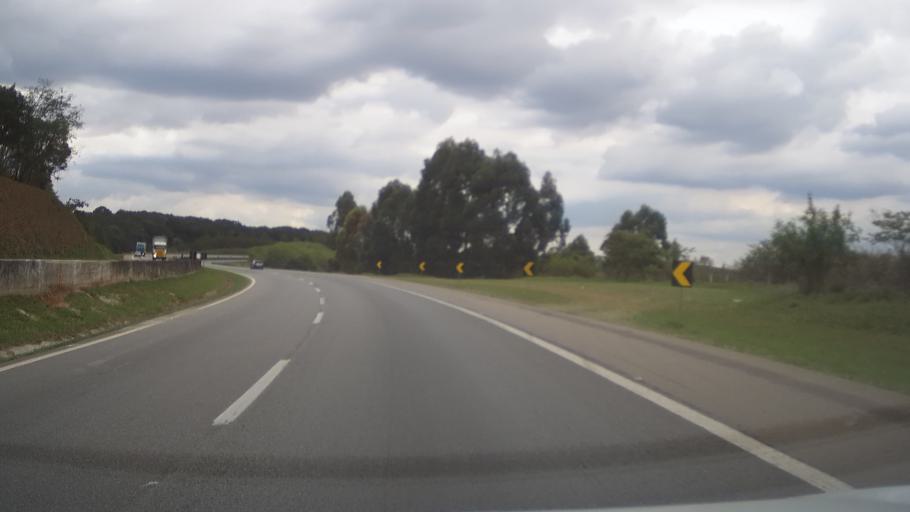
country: BR
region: Minas Gerais
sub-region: Tres Coracoes
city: Tres Coracoes
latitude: -21.4947
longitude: -45.2103
